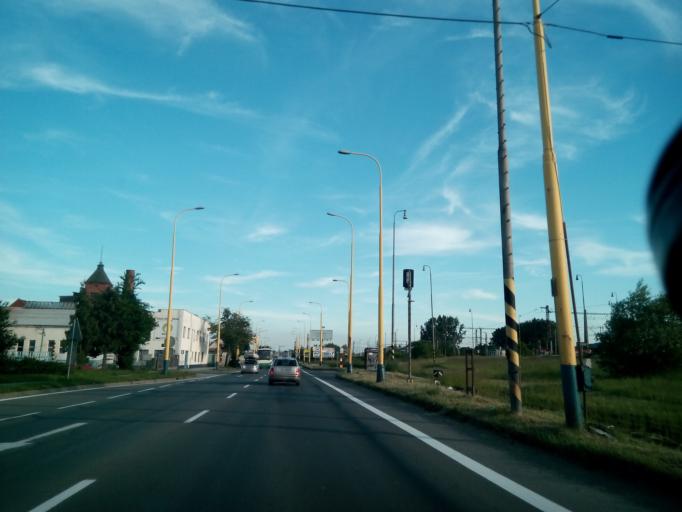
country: SK
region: Presovsky
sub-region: Okres Presov
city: Presov
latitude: 48.9796
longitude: 21.2509
